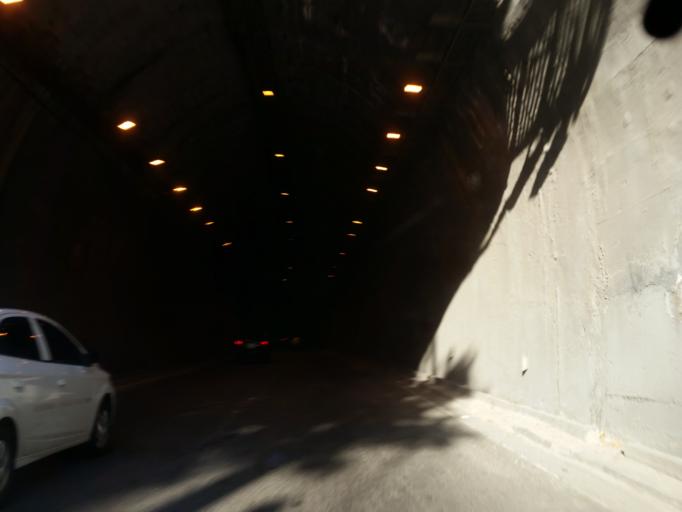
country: BR
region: Rio de Janeiro
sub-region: Rio De Janeiro
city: Rio de Janeiro
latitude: -22.9926
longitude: -43.2492
